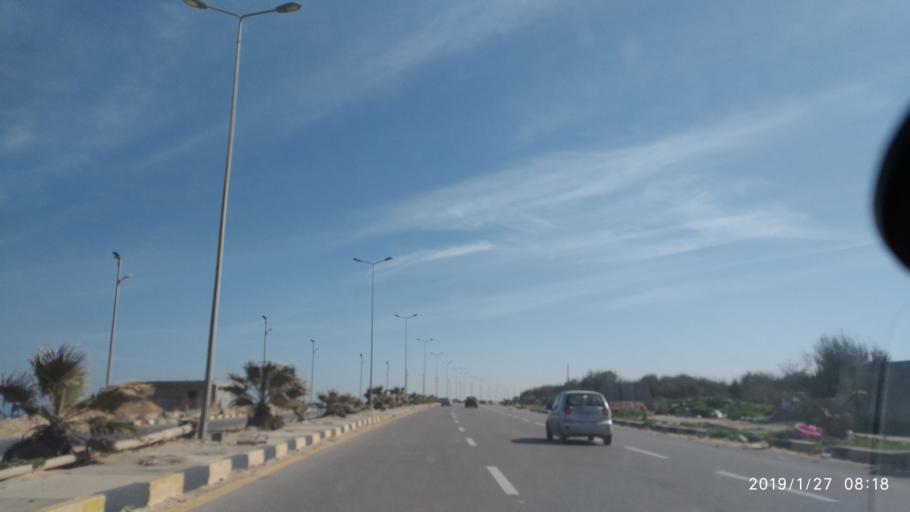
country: LY
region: Tripoli
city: Tagiura
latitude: 32.9019
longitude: 13.3063
